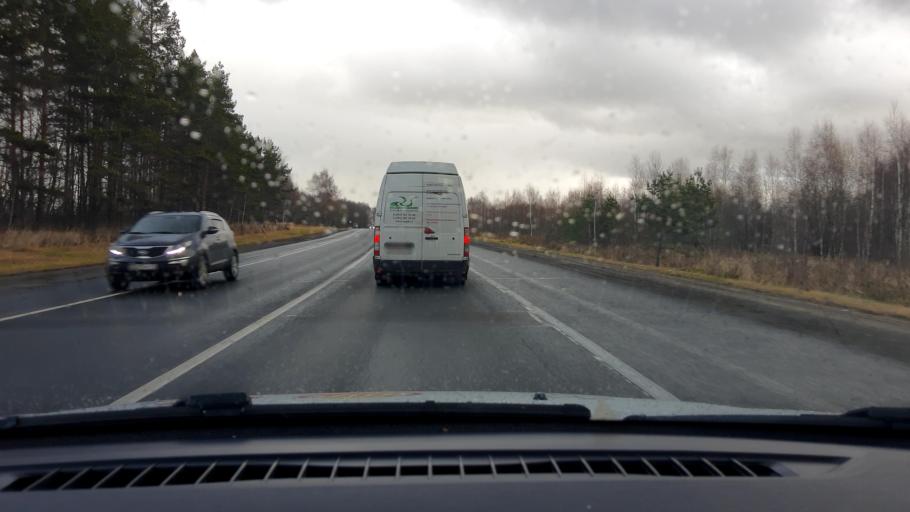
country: RU
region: Nizjnij Novgorod
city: Pervoye Maya
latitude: 55.9993
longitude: 44.7155
